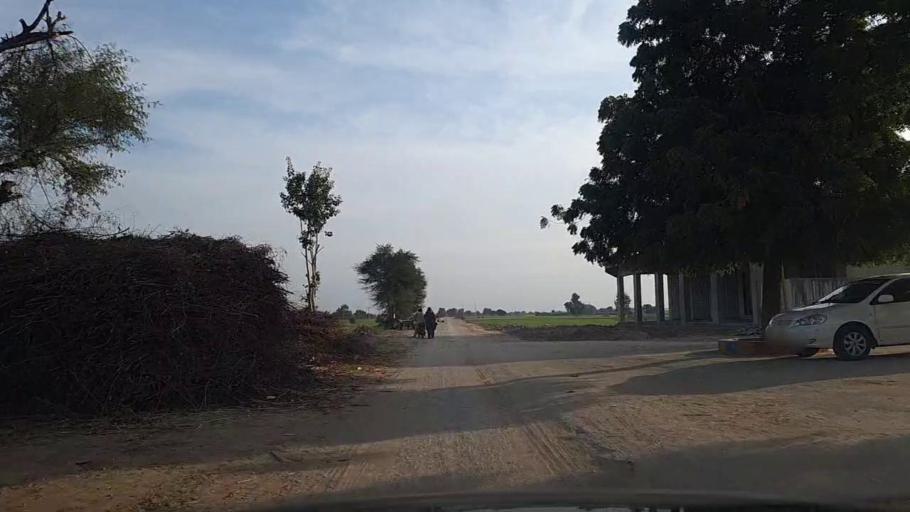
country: PK
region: Sindh
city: Jam Sahib
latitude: 26.4464
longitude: 68.5718
